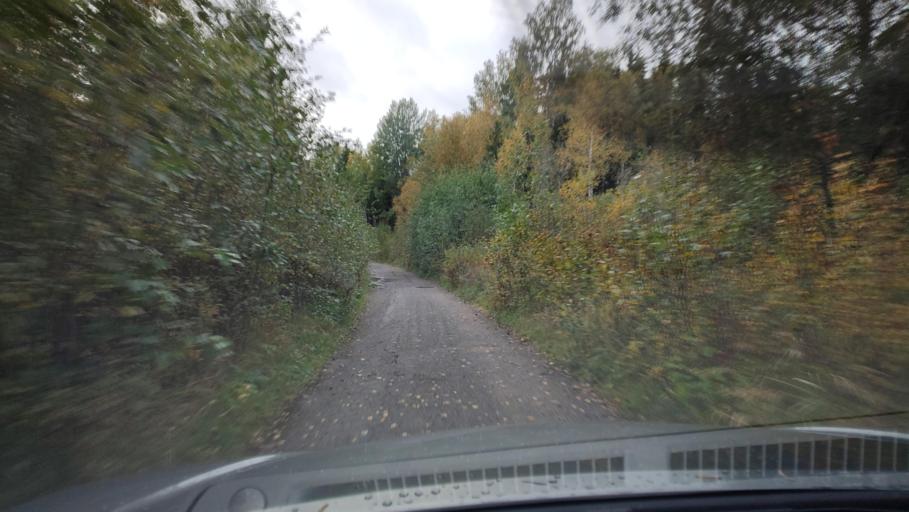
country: FI
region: Ostrobothnia
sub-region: Sydosterbotten
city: Kristinestad
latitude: 62.2721
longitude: 21.4459
